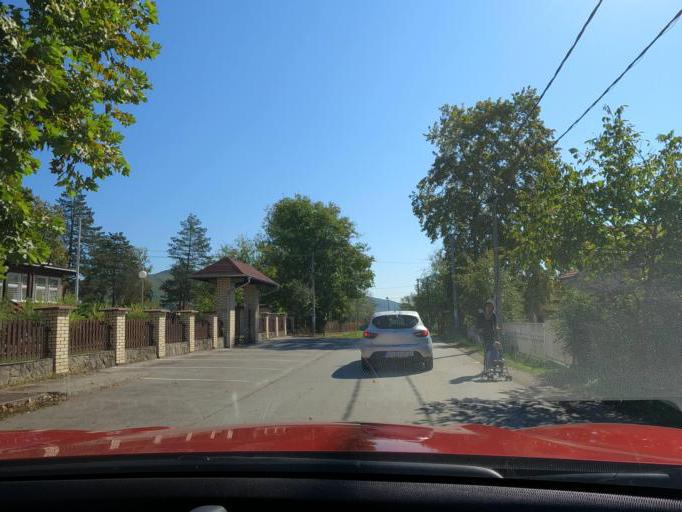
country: RS
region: Central Serbia
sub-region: Raski Okrug
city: Kraljevo
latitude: 43.7513
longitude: 20.7039
